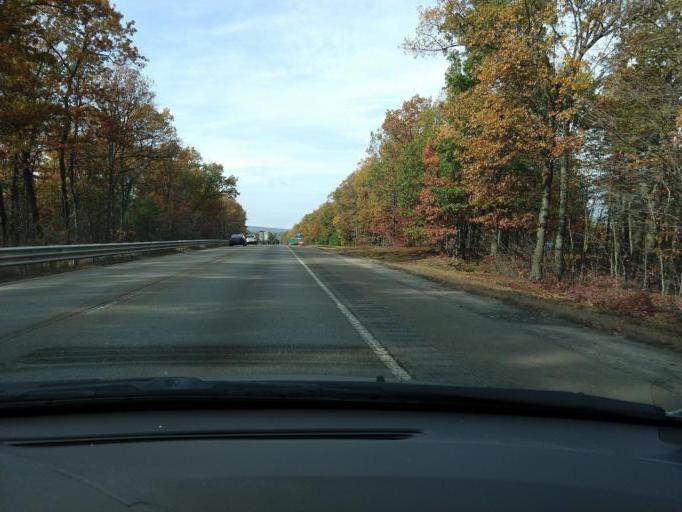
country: US
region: Massachusetts
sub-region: Middlesex County
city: Shirley
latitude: 42.5173
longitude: -71.6739
